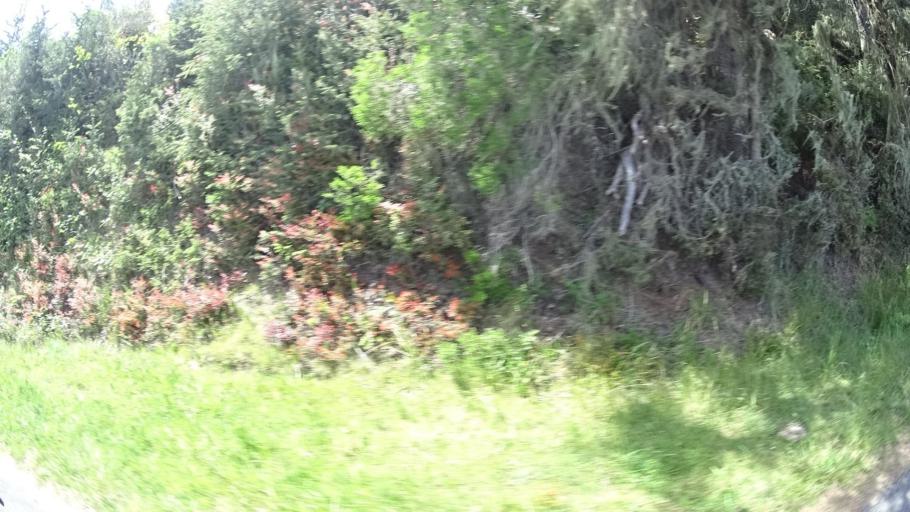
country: US
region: California
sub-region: Humboldt County
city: Humboldt Hill
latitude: 40.6782
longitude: -124.2280
